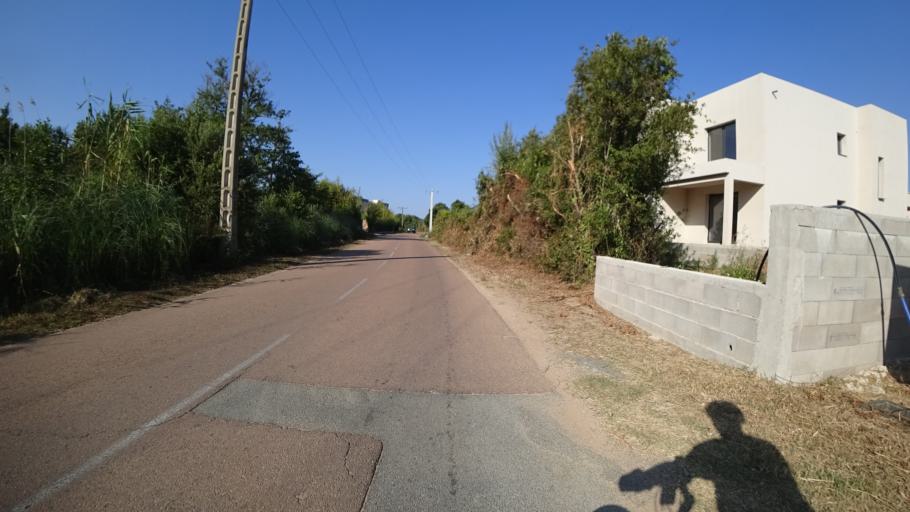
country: FR
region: Corsica
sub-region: Departement de la Corse-du-Sud
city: Porto-Vecchio
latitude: 41.6241
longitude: 9.3353
